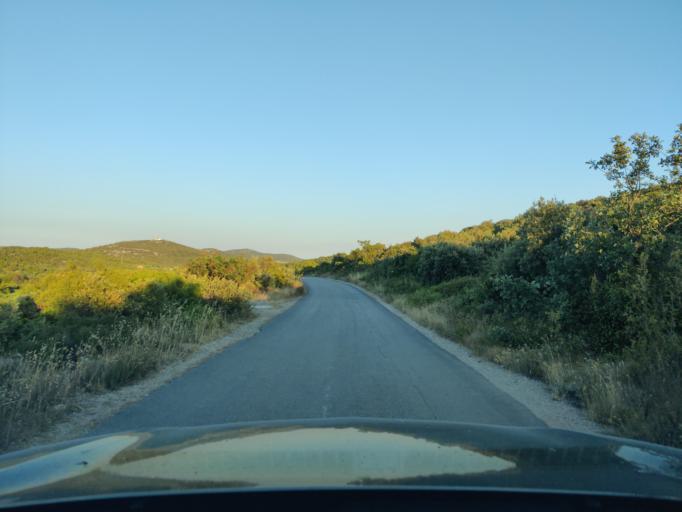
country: HR
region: Sibensko-Kniniska
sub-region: Grad Sibenik
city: Tisno
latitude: 43.8075
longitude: 15.6419
